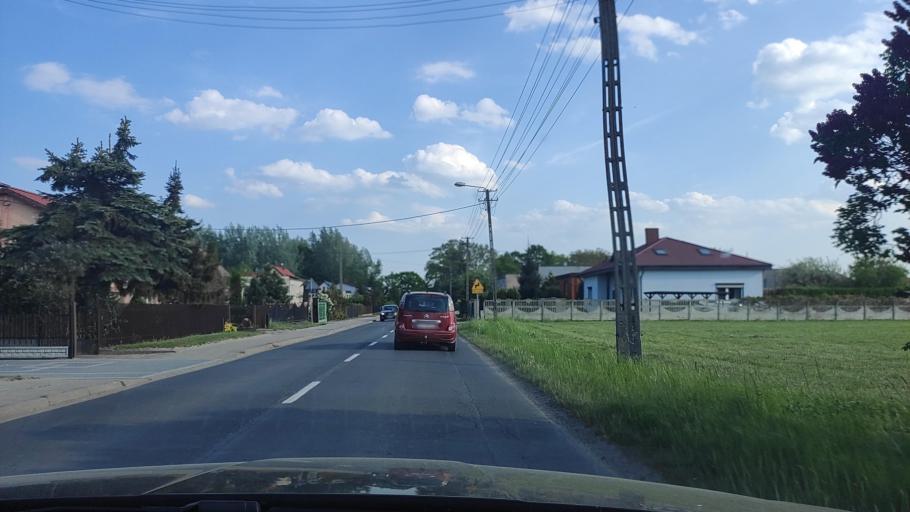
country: PL
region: Greater Poland Voivodeship
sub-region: Powiat poznanski
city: Kleszczewo
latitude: 52.3849
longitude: 17.1612
